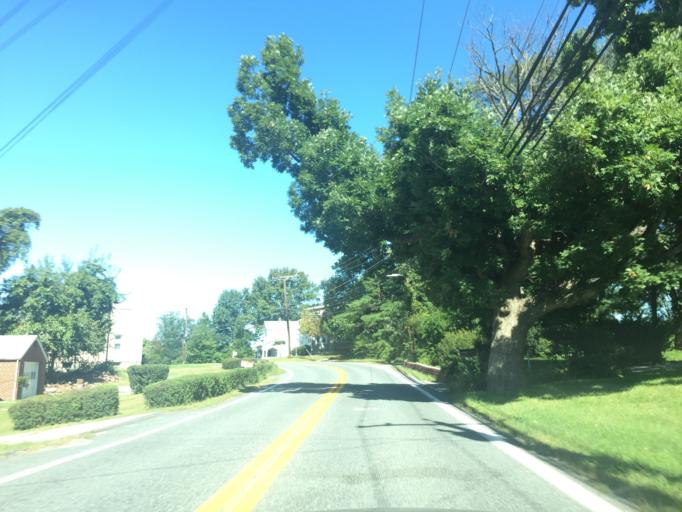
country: US
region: Maryland
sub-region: Baltimore County
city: Overlea
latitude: 39.3747
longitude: -76.5040
